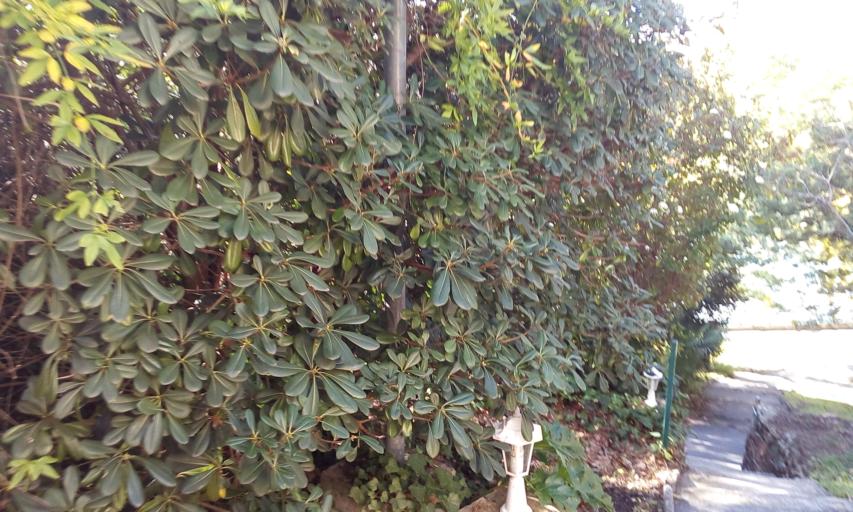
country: FR
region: Provence-Alpes-Cote d'Azur
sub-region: Departement du Var
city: Saint-Raphael
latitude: 43.4448
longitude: 6.7680
